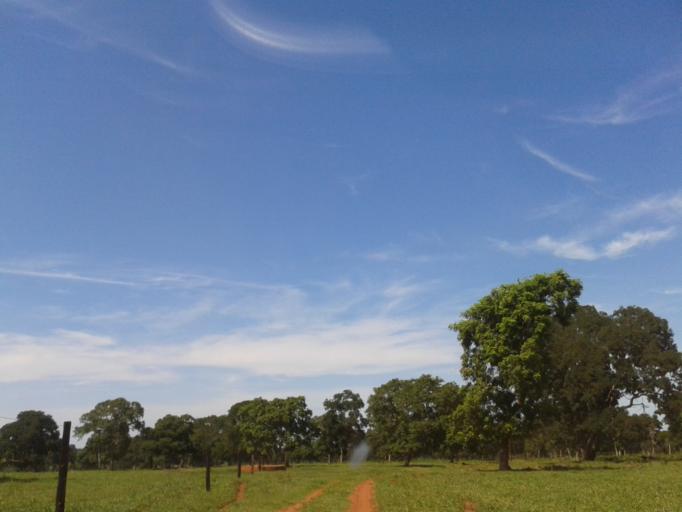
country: BR
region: Minas Gerais
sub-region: Santa Vitoria
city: Santa Vitoria
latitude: -19.1616
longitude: -50.5070
